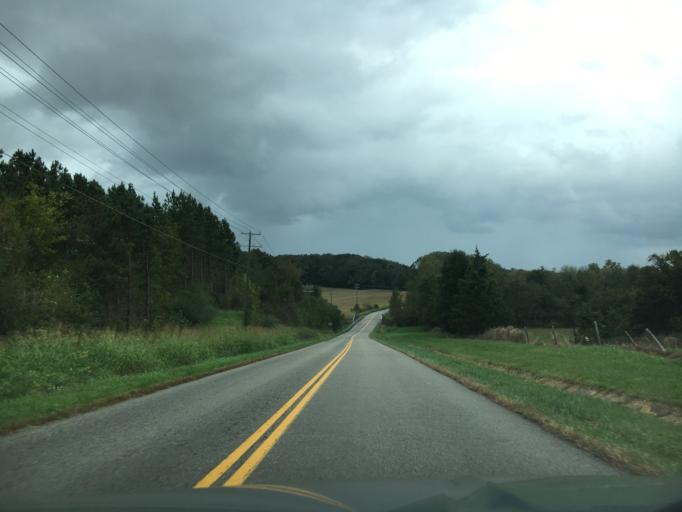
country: US
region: Virginia
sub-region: Amelia County
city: Amelia Court House
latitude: 37.3833
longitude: -77.9790
